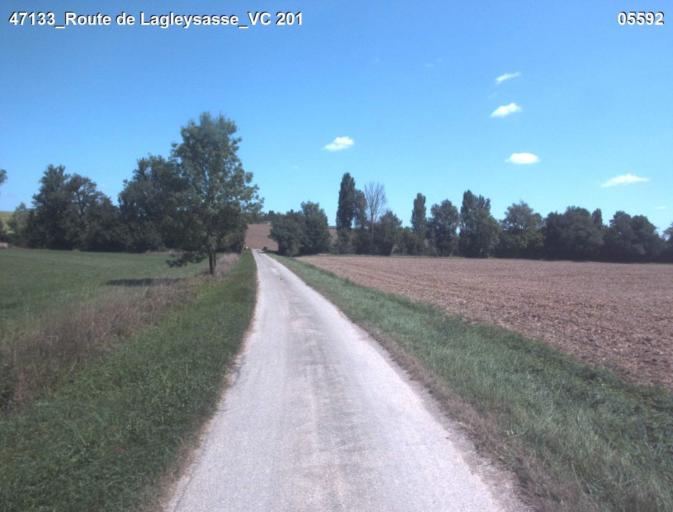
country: FR
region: Aquitaine
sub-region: Departement du Lot-et-Garonne
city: Laplume
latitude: 44.0658
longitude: 0.4957
